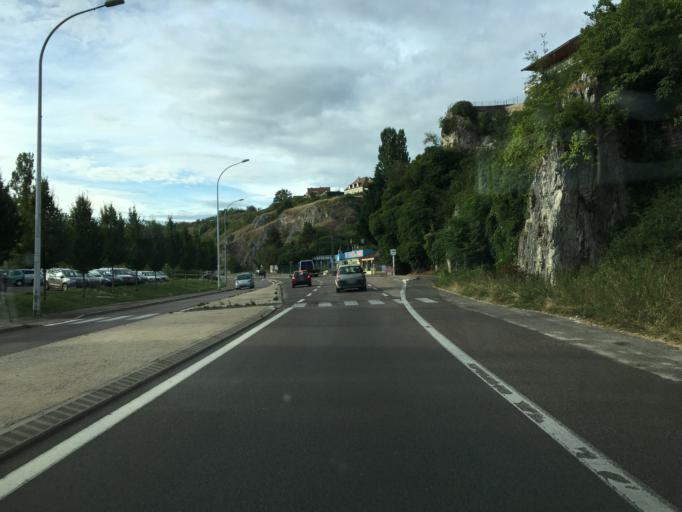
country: FR
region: Bourgogne
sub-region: Departement de la Cote-d'Or
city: Dijon
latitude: 47.3242
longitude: 5.0087
